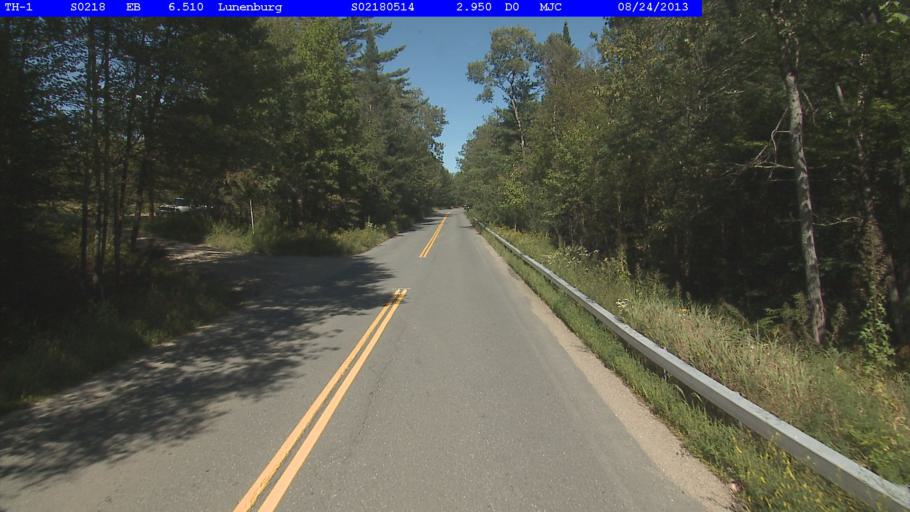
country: US
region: New Hampshire
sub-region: Coos County
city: Whitefield
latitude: 44.4191
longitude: -71.6977
